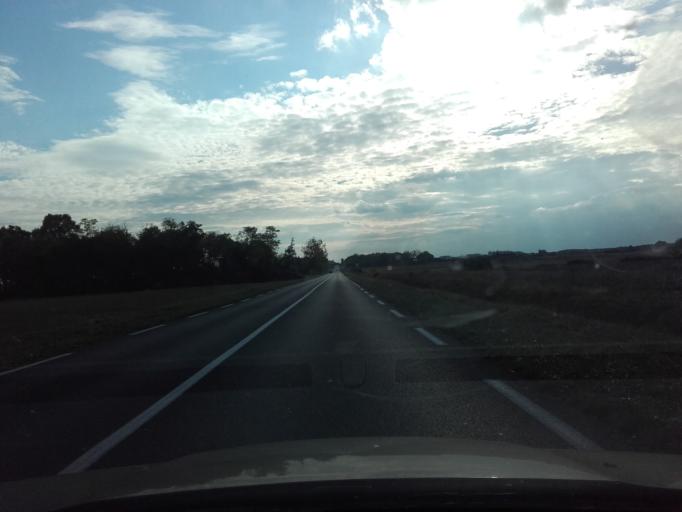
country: FR
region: Centre
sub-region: Departement d'Indre-et-Loire
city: Parcay-Meslay
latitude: 47.4601
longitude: 0.7402
